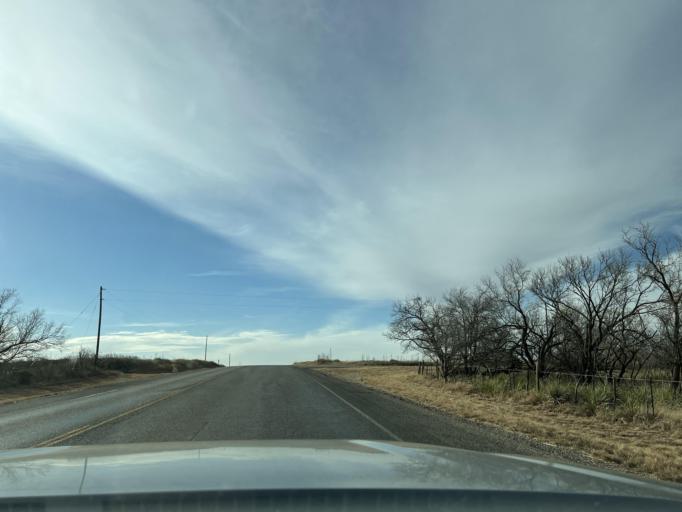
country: US
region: Texas
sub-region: Fisher County
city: Rotan
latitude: 32.7395
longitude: -100.5254
